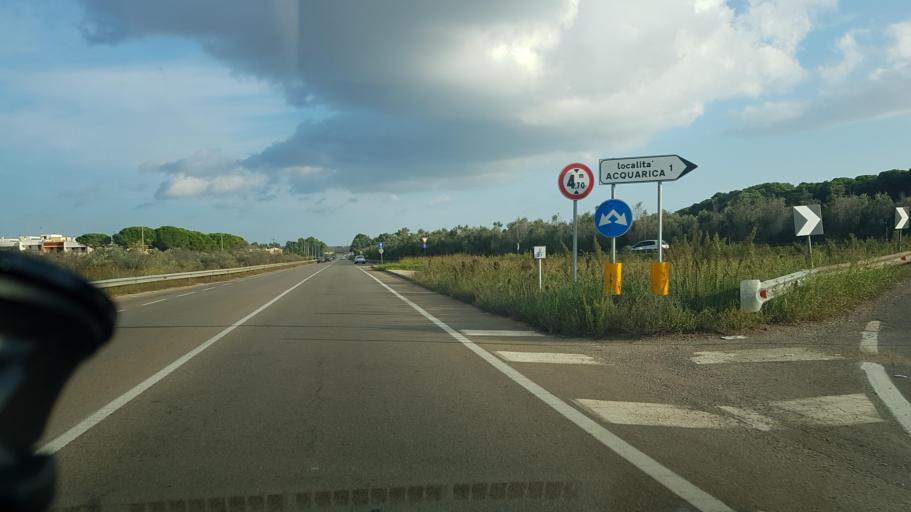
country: IT
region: Apulia
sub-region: Provincia di Lecce
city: Acquarica del Capo
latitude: 39.9002
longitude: 18.2500
